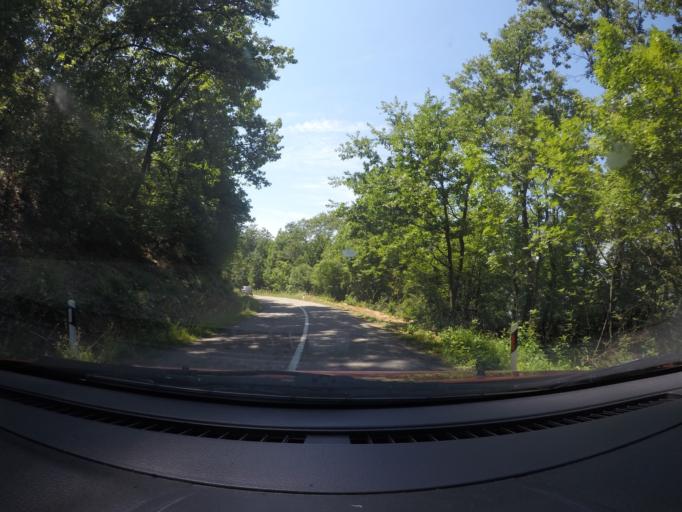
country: RO
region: Mehedinti
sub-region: Comuna Svinita
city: Svinita
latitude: 44.4739
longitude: 22.1030
